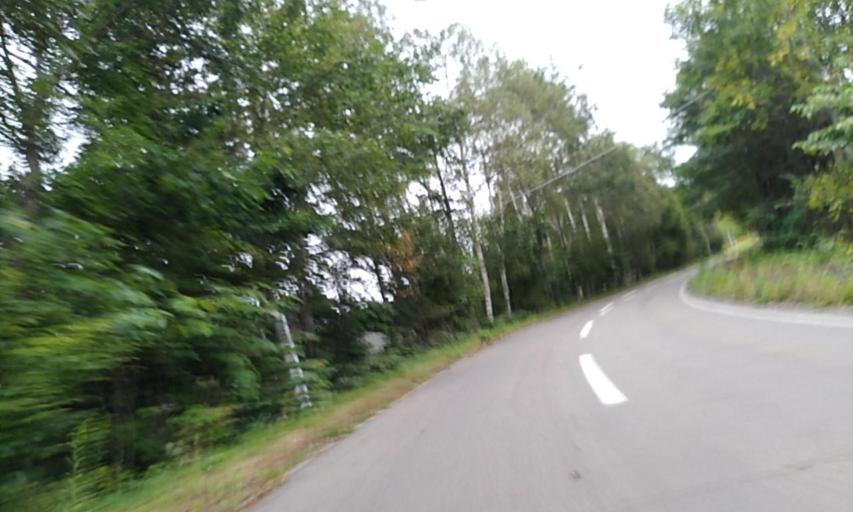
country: JP
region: Hokkaido
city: Obihiro
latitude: 42.6721
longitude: 143.0413
